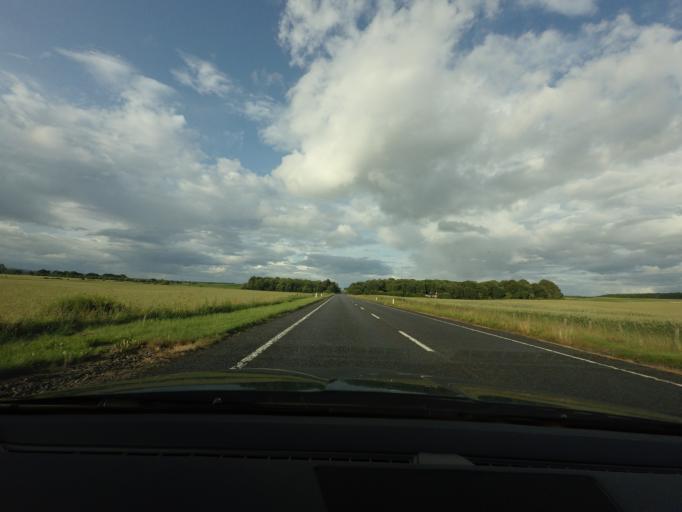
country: GB
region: Scotland
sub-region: Highland
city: Fortrose
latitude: 57.5367
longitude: -4.0251
